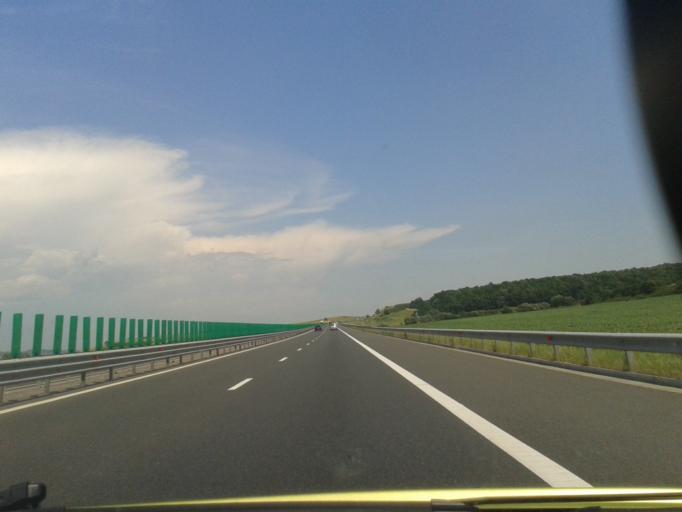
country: RO
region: Alba
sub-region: Comuna Blandiana
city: Blandiana
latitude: 45.9513
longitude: 23.4267
